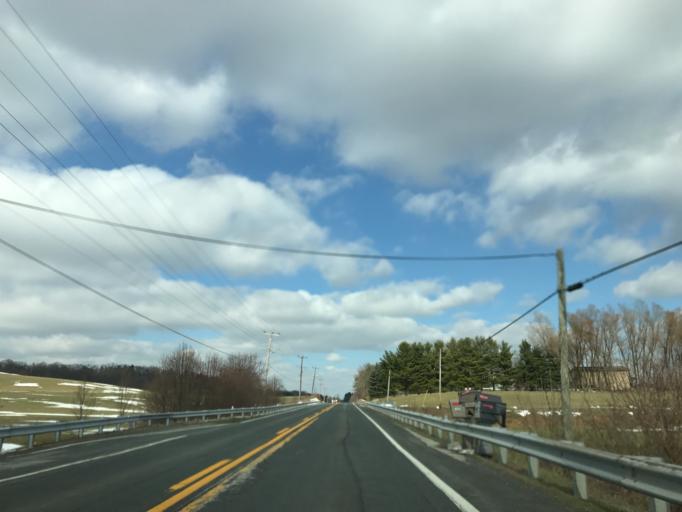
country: US
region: Maryland
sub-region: Carroll County
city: Manchester
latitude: 39.6923
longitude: -76.9129
